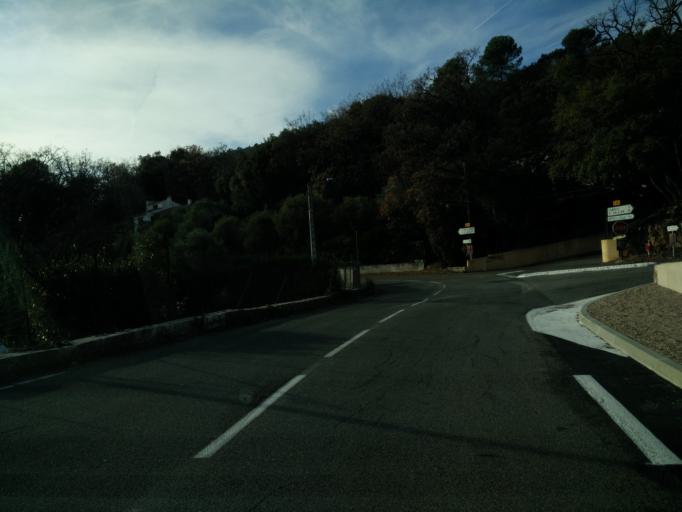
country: FR
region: Provence-Alpes-Cote d'Azur
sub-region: Departement des Alpes-Maritimes
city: Speracedes
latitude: 43.6461
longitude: 6.8547
